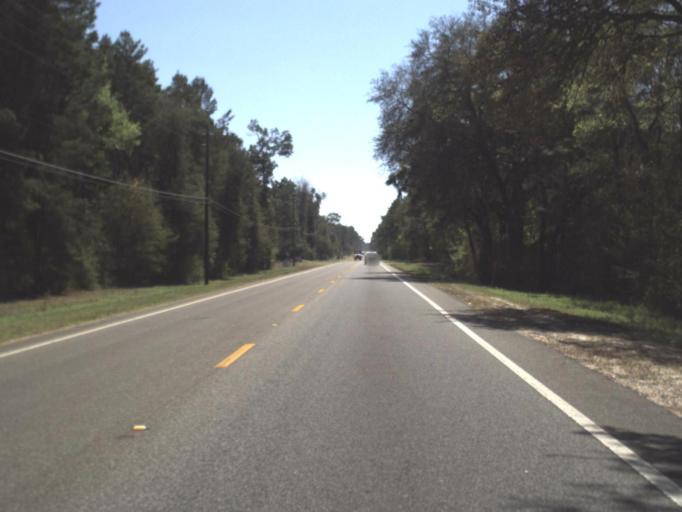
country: US
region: Florida
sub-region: Leon County
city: Woodville
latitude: 30.3551
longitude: -84.2611
